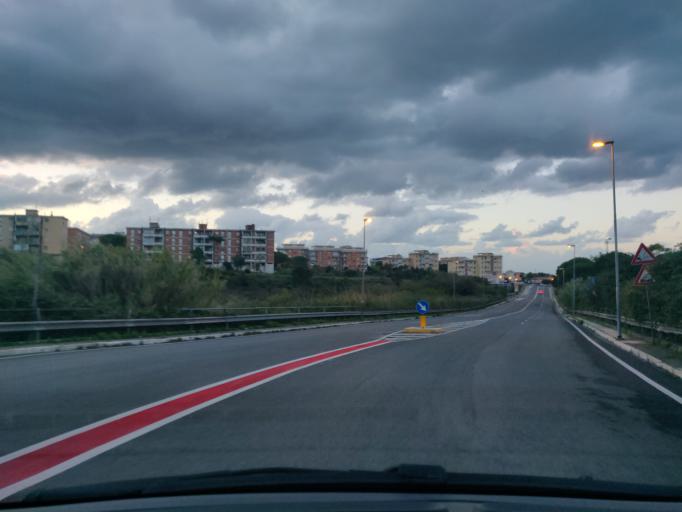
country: IT
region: Latium
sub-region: Citta metropolitana di Roma Capitale
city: Civitavecchia
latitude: 42.0848
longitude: 11.8088
